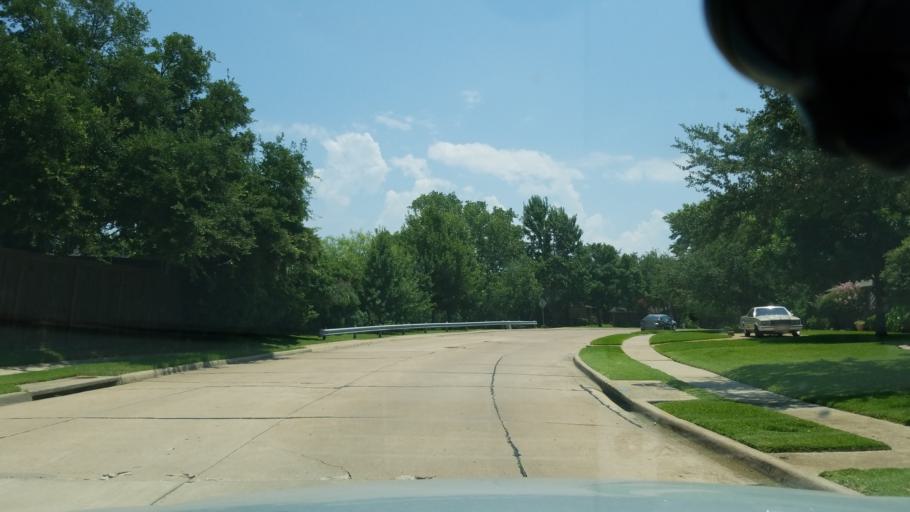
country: US
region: Texas
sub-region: Dallas County
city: Coppell
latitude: 32.9631
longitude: -96.9981
